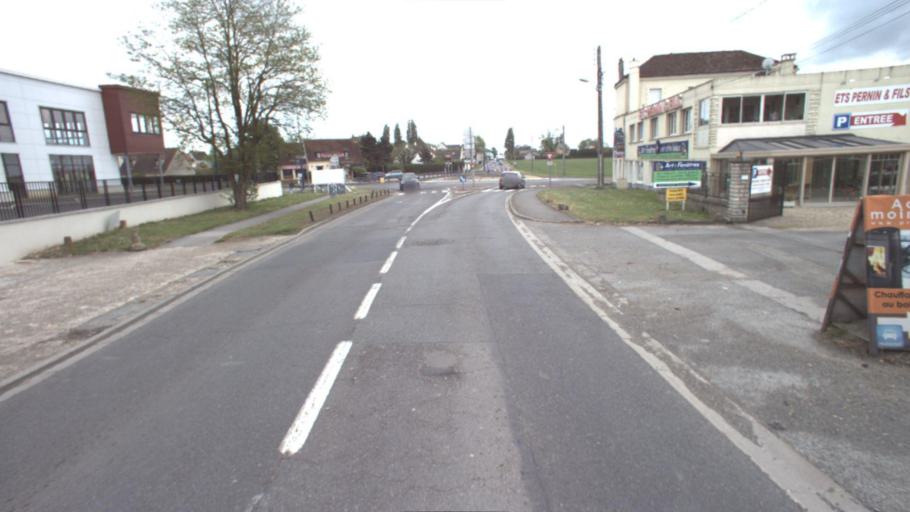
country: FR
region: Picardie
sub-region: Departement de l'Oise
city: Lagny-le-Sec
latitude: 49.0945
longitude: 2.7458
